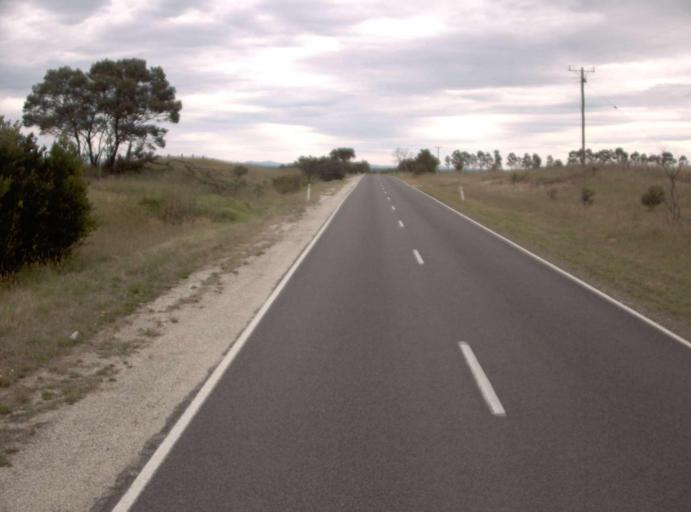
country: AU
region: Victoria
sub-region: Wellington
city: Sale
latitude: -38.0587
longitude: 147.1479
